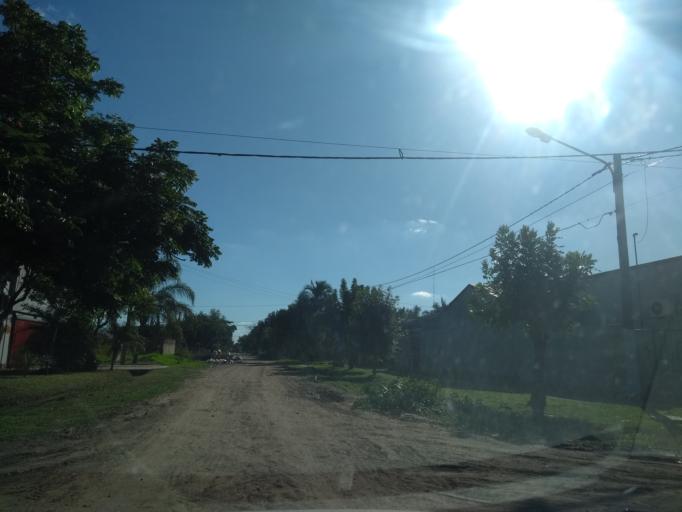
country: AR
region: Chaco
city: Resistencia
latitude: -27.4758
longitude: -58.9831
